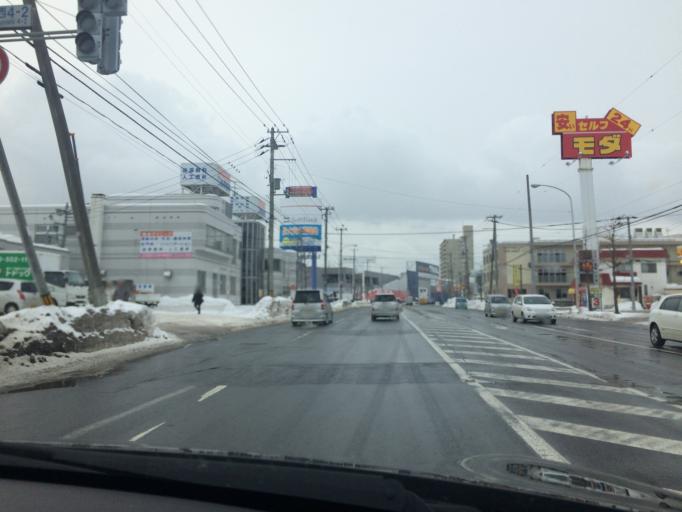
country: JP
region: Hokkaido
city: Ebetsu
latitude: 43.0524
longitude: 141.4595
